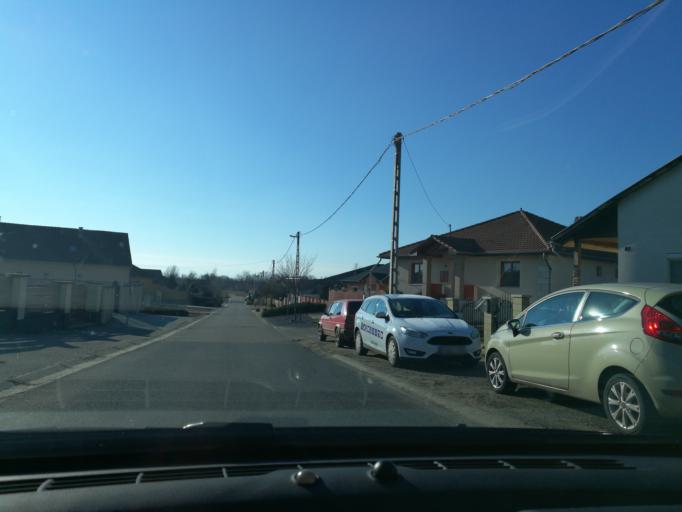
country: HU
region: Szabolcs-Szatmar-Bereg
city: Nyiregyhaza
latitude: 47.9236
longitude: 21.7545
